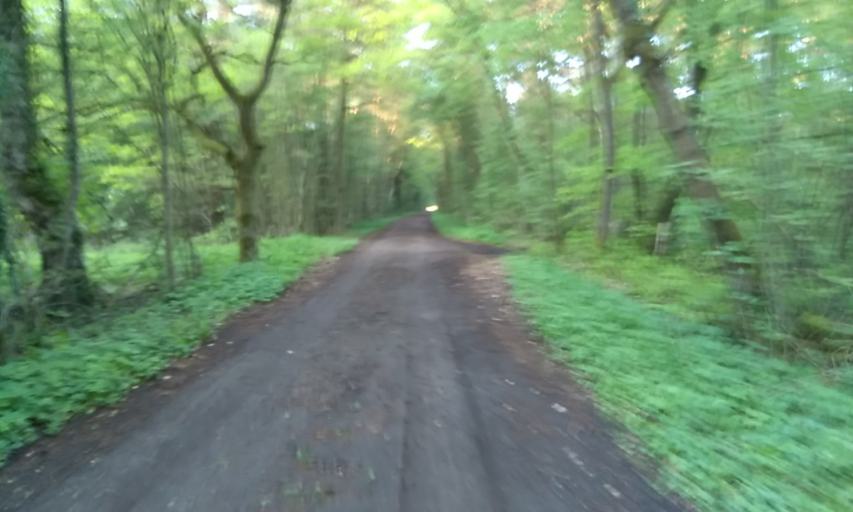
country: DE
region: Lower Saxony
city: Harsefeld
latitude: 53.4134
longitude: 9.5035
